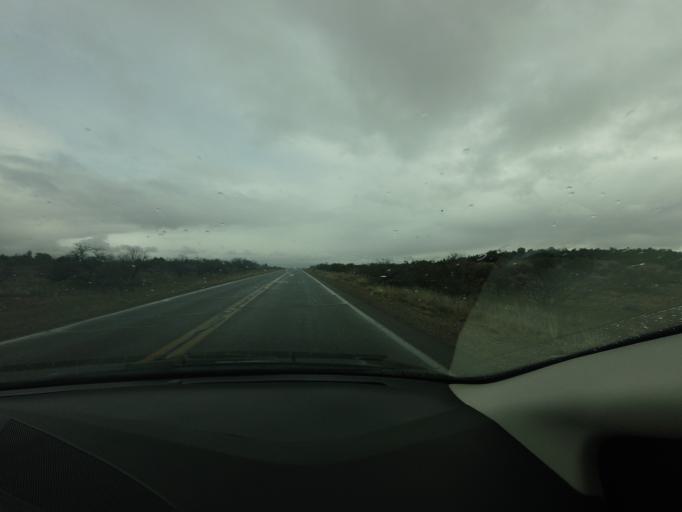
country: US
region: Arizona
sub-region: Yavapai County
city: Cornville
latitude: 34.6896
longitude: -111.8525
